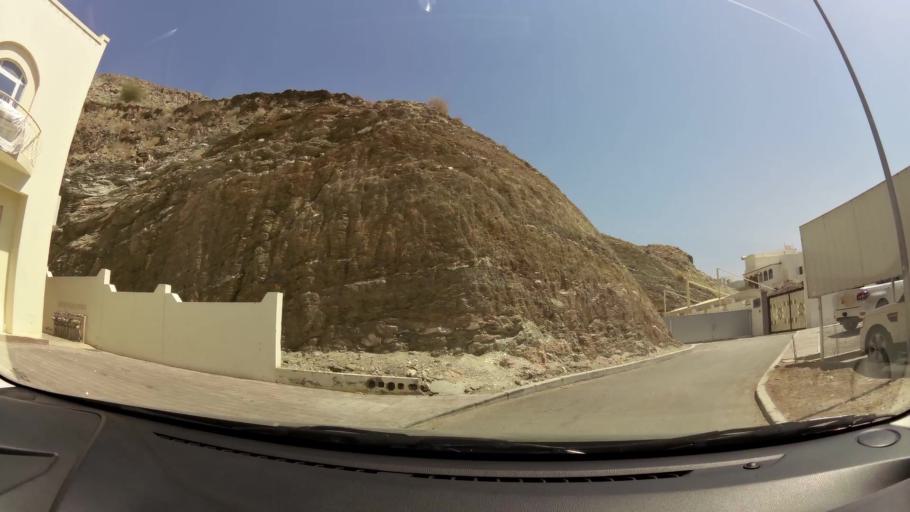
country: OM
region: Muhafazat Masqat
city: Muscat
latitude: 23.5974
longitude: 58.5334
